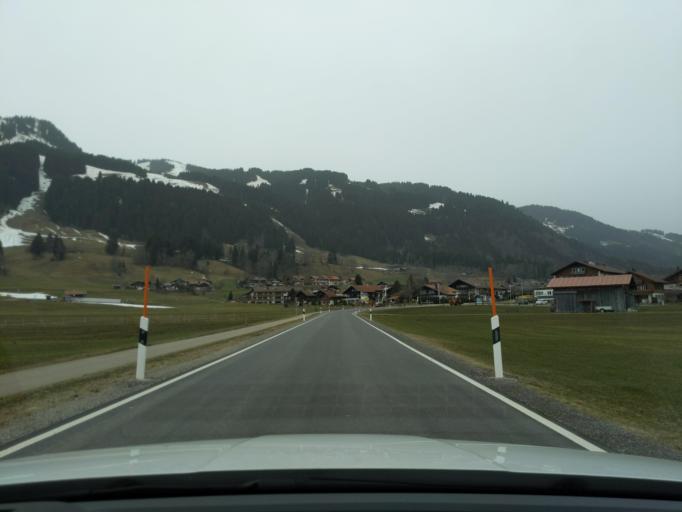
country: DE
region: Bavaria
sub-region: Swabia
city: Obermaiselstein
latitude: 47.4570
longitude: 10.2371
